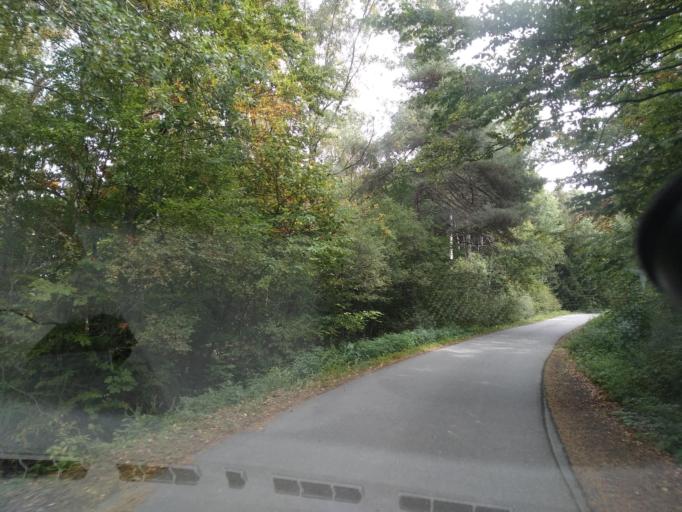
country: PL
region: Lesser Poland Voivodeship
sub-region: Powiat gorlicki
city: Uscie Gorlickie
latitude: 49.5397
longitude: 21.2128
